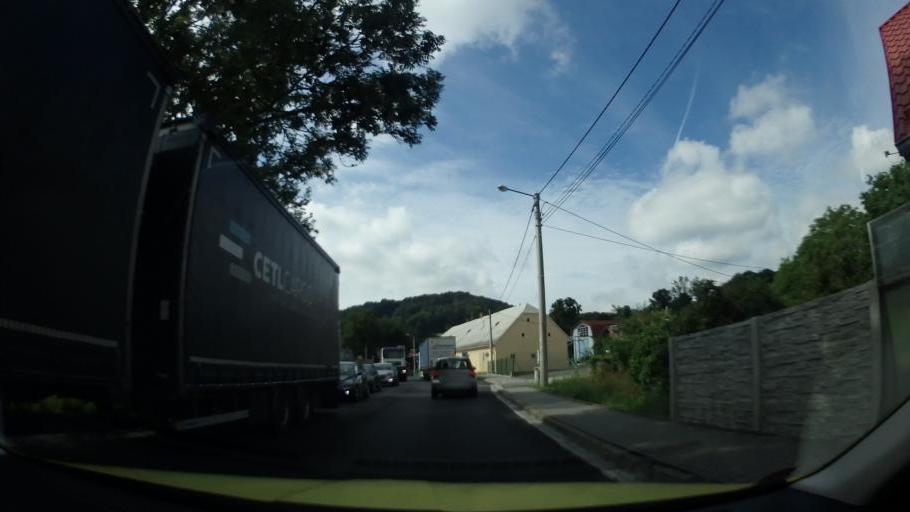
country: CZ
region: Moravskoslezsky
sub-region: Okres Novy Jicin
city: Novy Jicin
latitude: 49.5750
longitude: 18.0211
